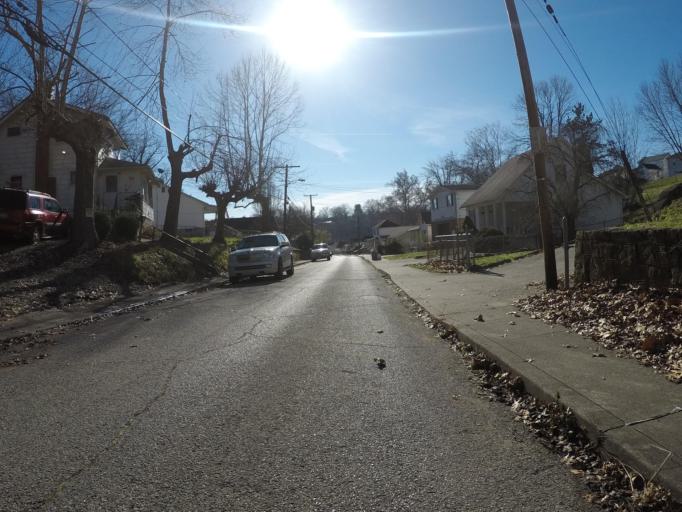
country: US
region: West Virginia
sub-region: Cabell County
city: Huntington
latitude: 38.4120
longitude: -82.3984
